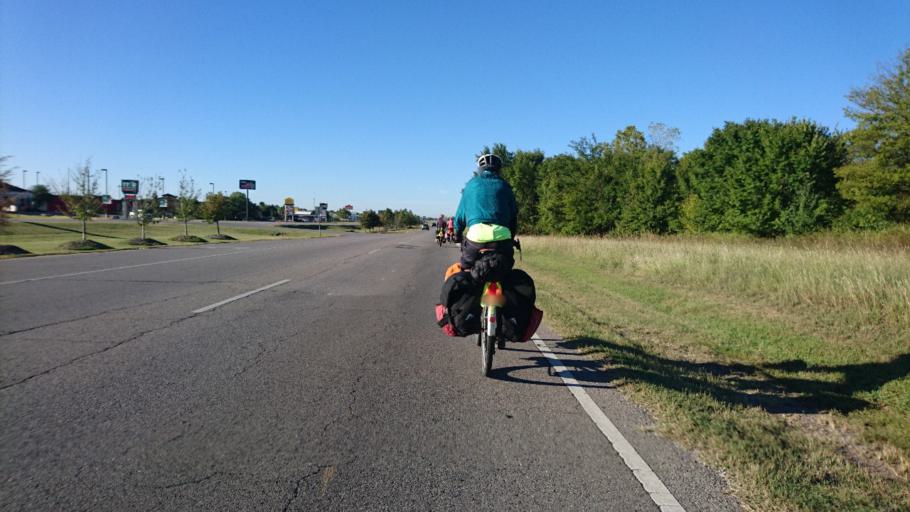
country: US
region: Oklahoma
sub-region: Rogers County
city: Claremore
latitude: 36.2889
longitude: -95.6339
